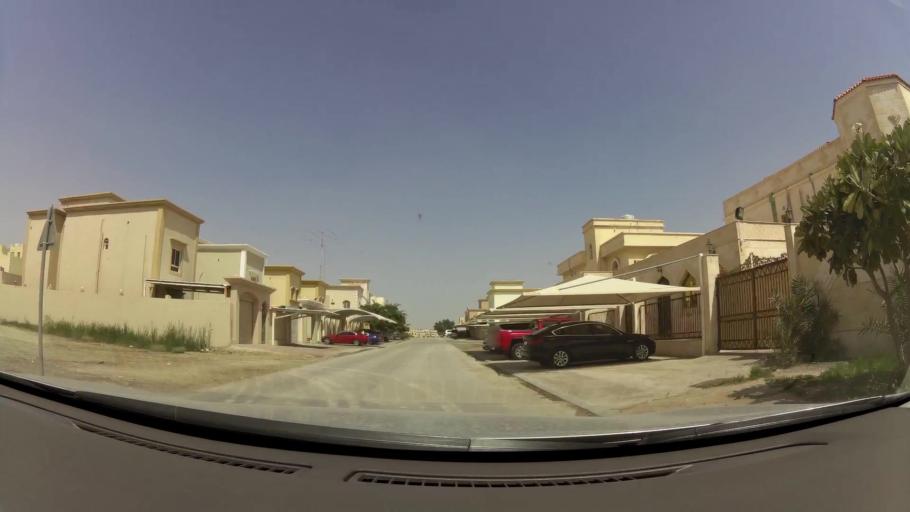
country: QA
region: Baladiyat Umm Salal
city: Umm Salal Muhammad
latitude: 25.3789
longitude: 51.4251
